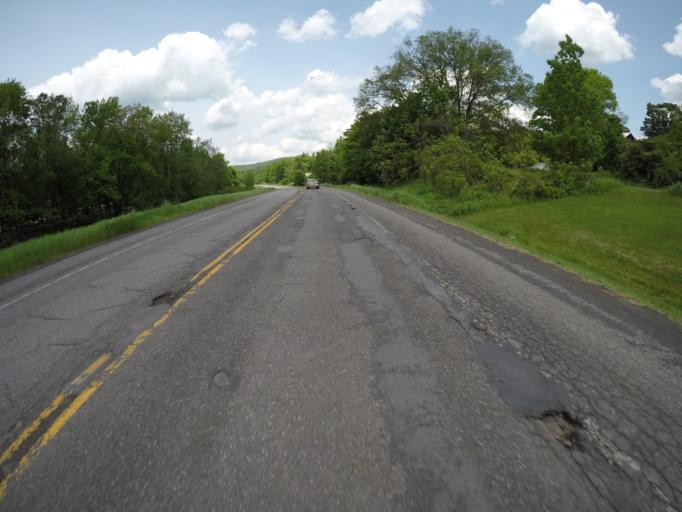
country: US
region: New York
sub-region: Delaware County
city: Stamford
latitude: 42.1803
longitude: -74.6004
